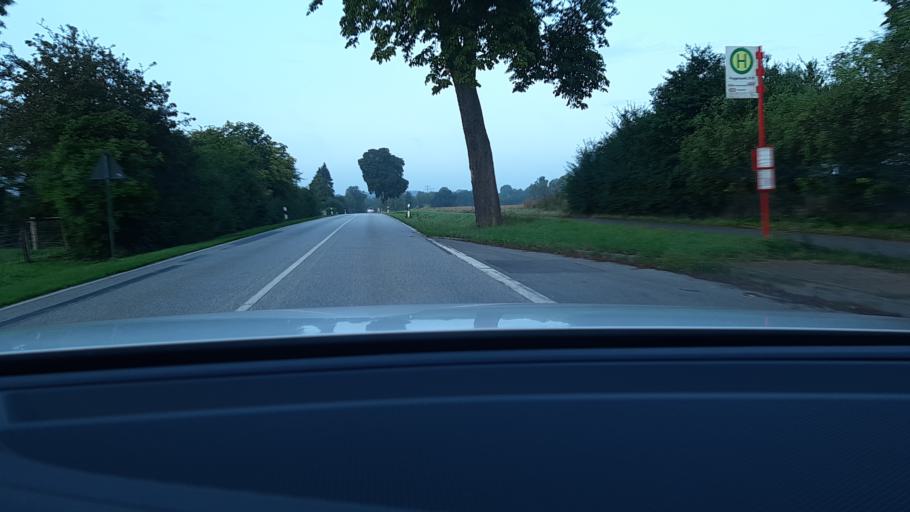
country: DE
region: Schleswig-Holstein
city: Hamberge
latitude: 53.8473
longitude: 10.6123
